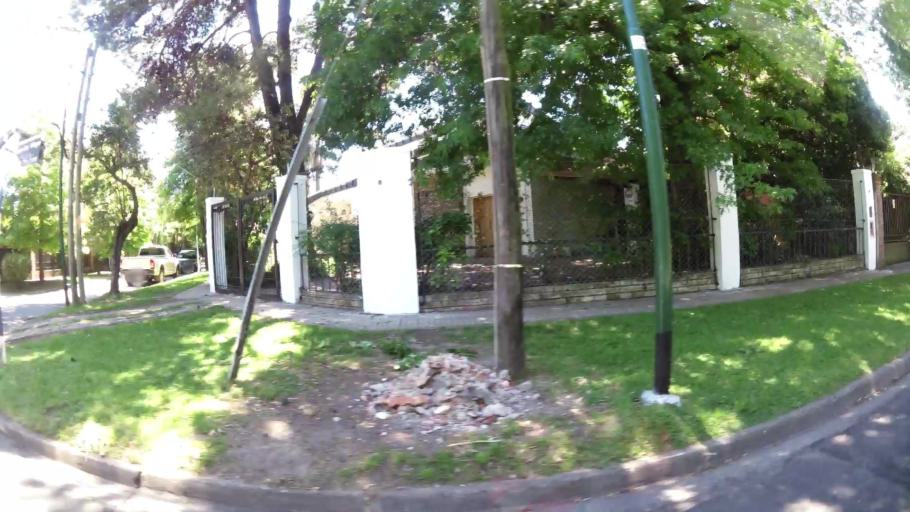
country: AR
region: Buenos Aires
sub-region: Partido de San Isidro
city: San Isidro
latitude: -34.5006
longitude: -58.5618
